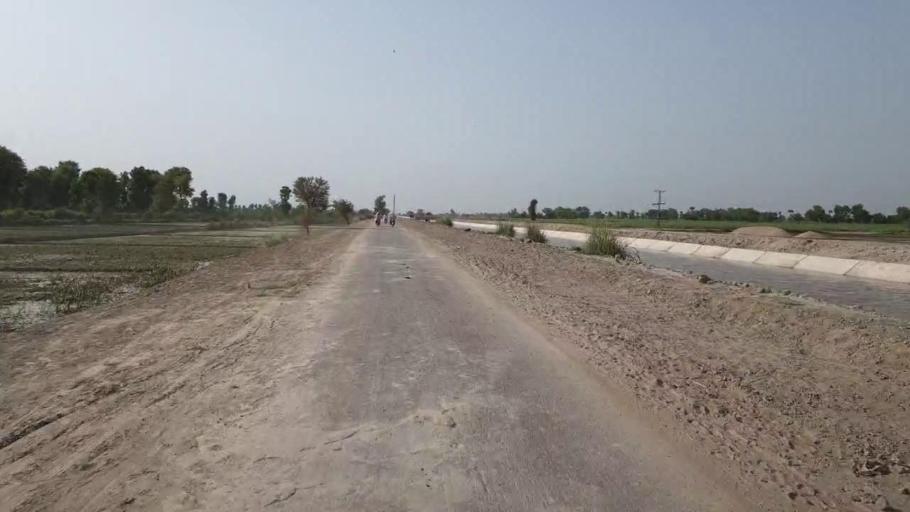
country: PK
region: Sindh
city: Daur
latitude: 26.3347
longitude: 68.1641
